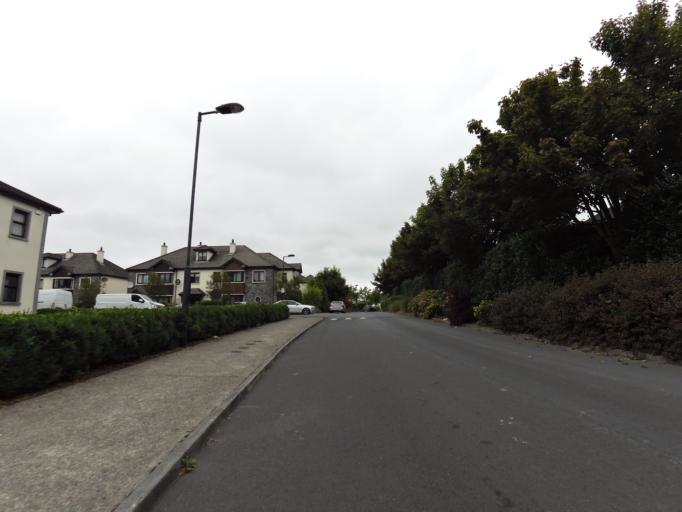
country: IE
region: Connaught
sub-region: County Galway
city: Loughrea
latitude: 53.2048
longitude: -8.5612
